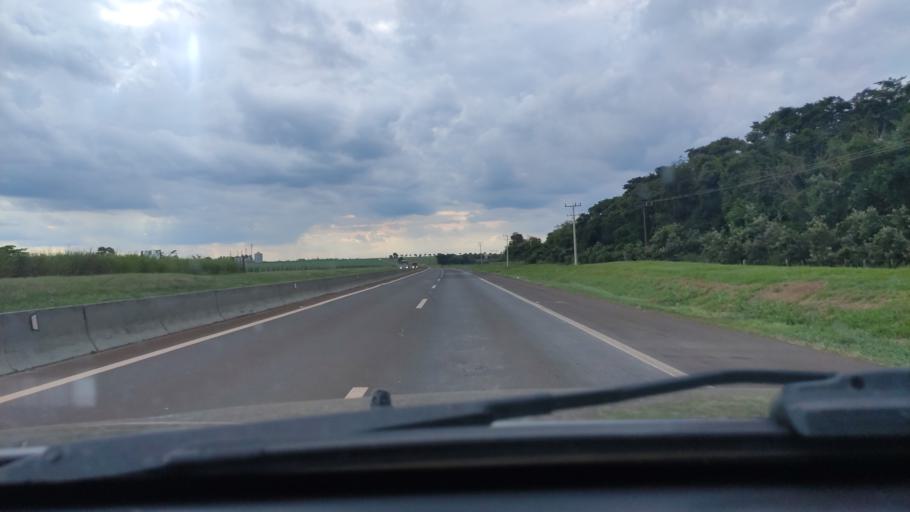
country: BR
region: Sao Paulo
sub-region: Palmital
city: Palmital
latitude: -22.8322
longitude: -50.0255
